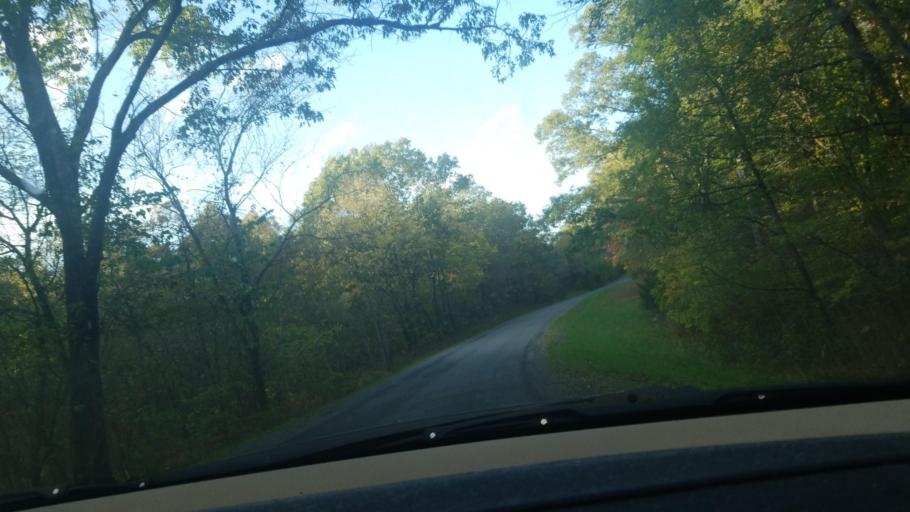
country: US
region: Illinois
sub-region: Saline County
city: Carrier Mills
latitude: 37.7749
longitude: -88.7149
